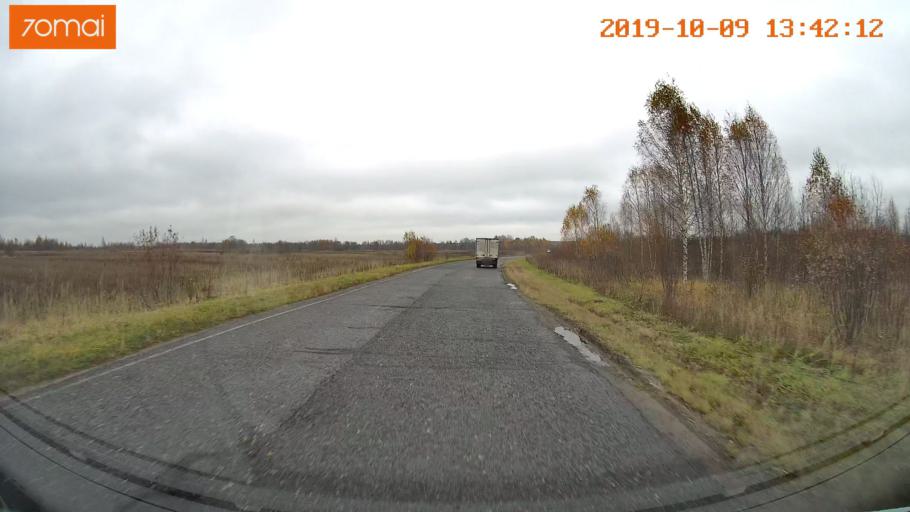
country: RU
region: Kostroma
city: Buy
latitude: 58.3543
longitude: 41.1843
